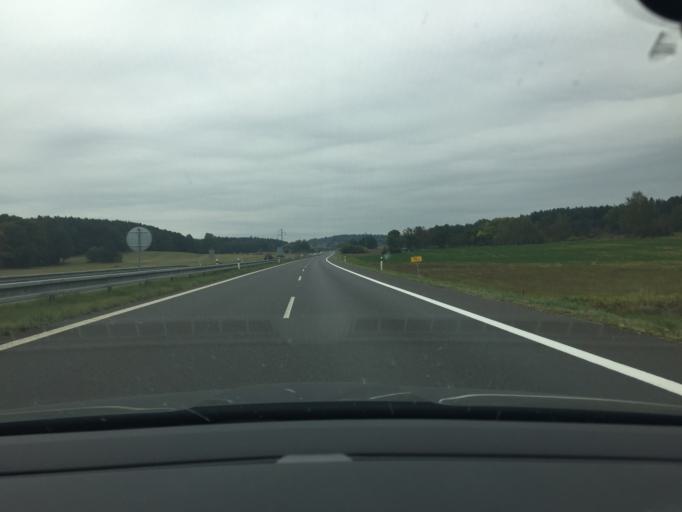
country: CZ
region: Jihocesky
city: Mirotice
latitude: 49.4082
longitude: 14.0397
